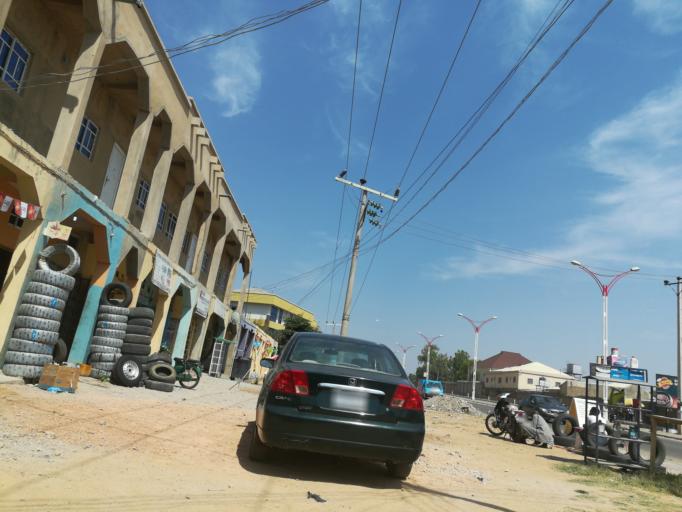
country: NG
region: Kano
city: Kano
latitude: 12.0294
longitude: 8.5152
